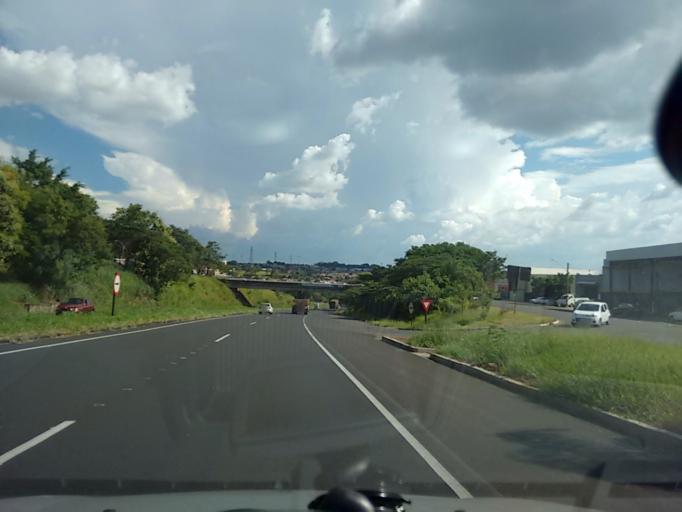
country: BR
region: Sao Paulo
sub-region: Marilia
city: Marilia
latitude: -22.2102
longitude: -49.9632
